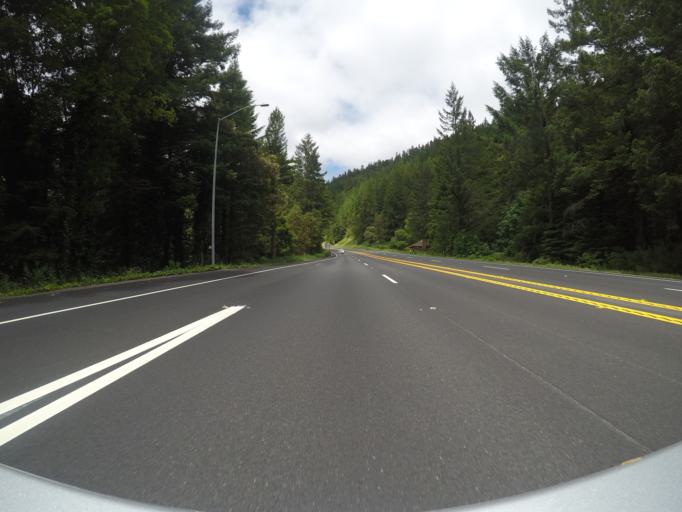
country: US
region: California
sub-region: Humboldt County
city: Redway
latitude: 40.3245
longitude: -123.9216
